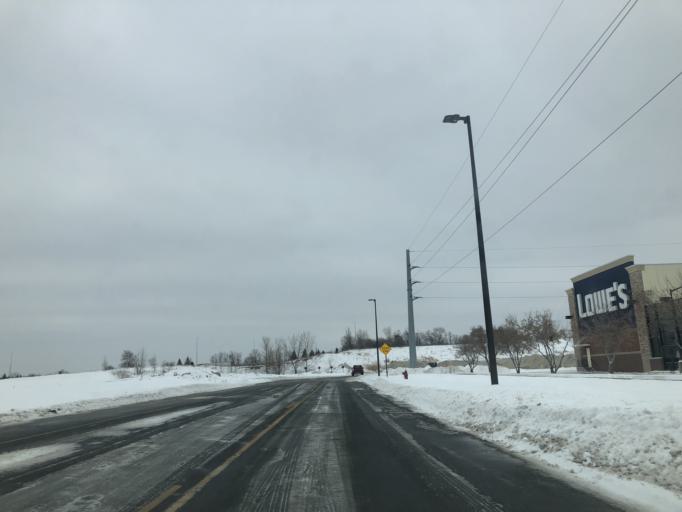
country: US
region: Minnesota
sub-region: Hennepin County
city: Osseo
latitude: 45.0902
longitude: -93.4214
